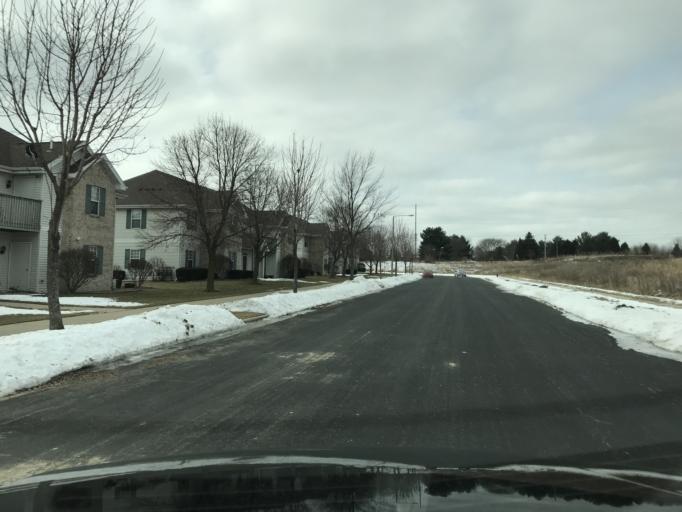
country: US
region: Wisconsin
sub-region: Dane County
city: Cottage Grove
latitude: 43.0984
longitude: -89.2640
